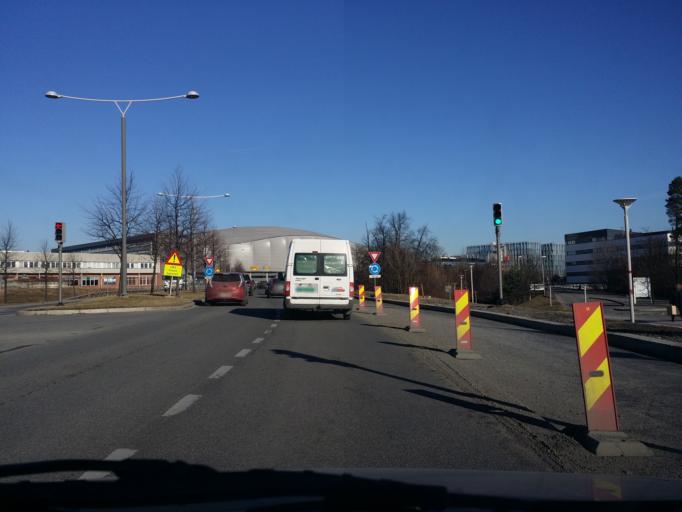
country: NO
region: Akershus
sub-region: Baerum
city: Lysaker
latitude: 59.8999
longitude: 10.6258
